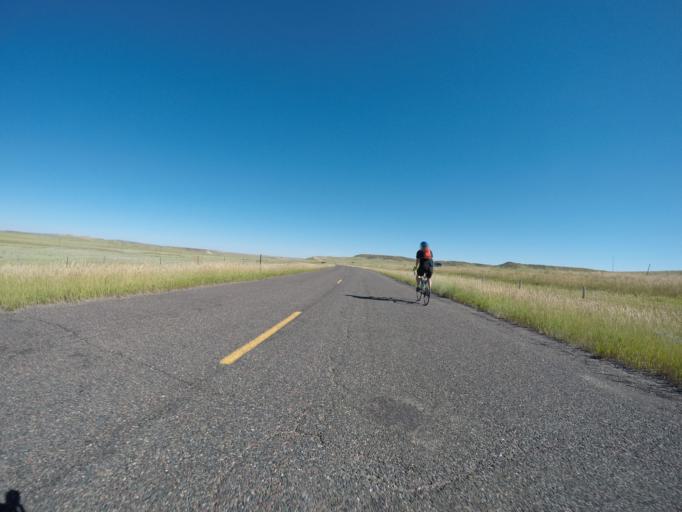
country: US
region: Wyoming
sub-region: Platte County
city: Wheatland
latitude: 41.6985
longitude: -104.8295
